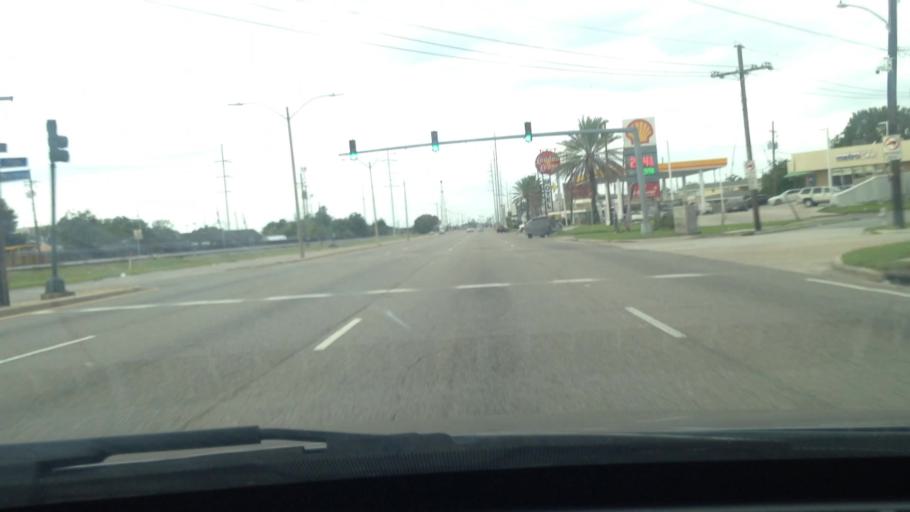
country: US
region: Louisiana
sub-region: Jefferson Parish
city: Jefferson
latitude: 29.9718
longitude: -90.1201
